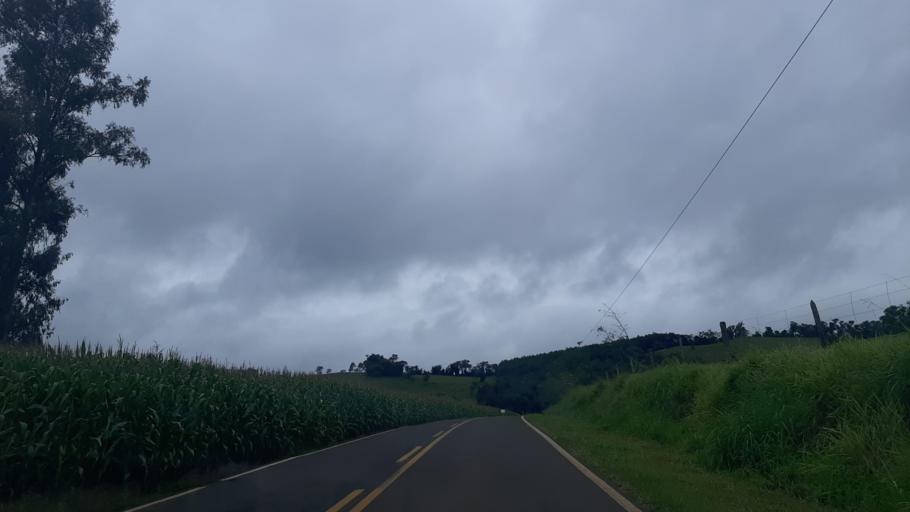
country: BR
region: Parana
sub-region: Ampere
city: Ampere
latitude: -25.9805
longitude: -53.4437
